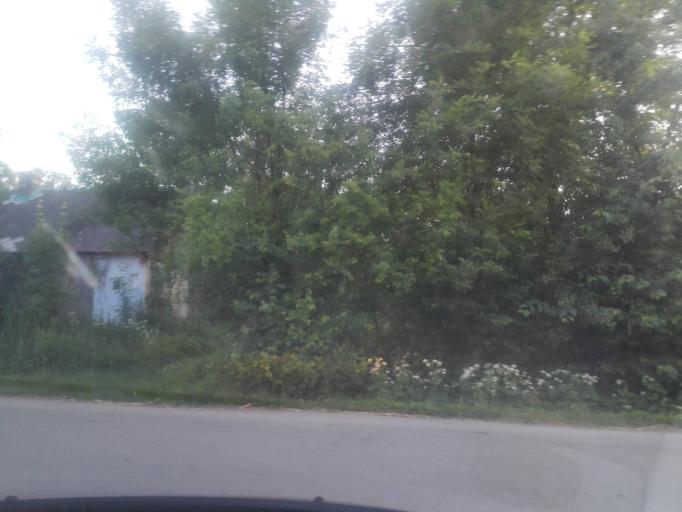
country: PL
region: Swietokrzyskie
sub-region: Powiat jedrzejowski
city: Slupia
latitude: 50.6493
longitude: 19.9225
